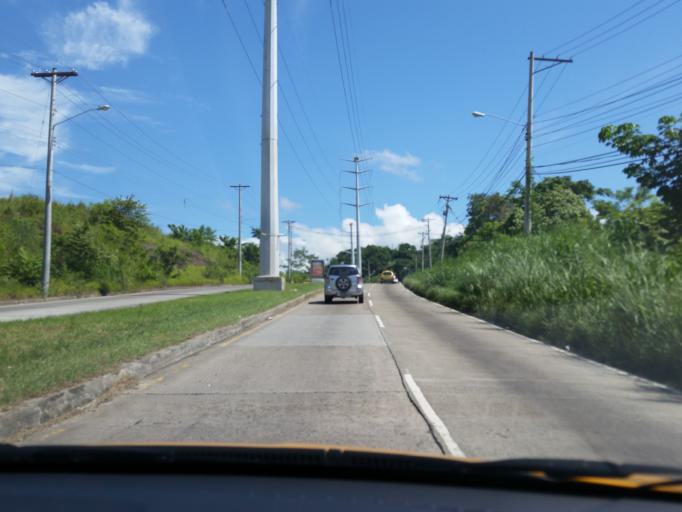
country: PA
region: Panama
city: San Miguelito
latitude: 9.0628
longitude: -79.4621
